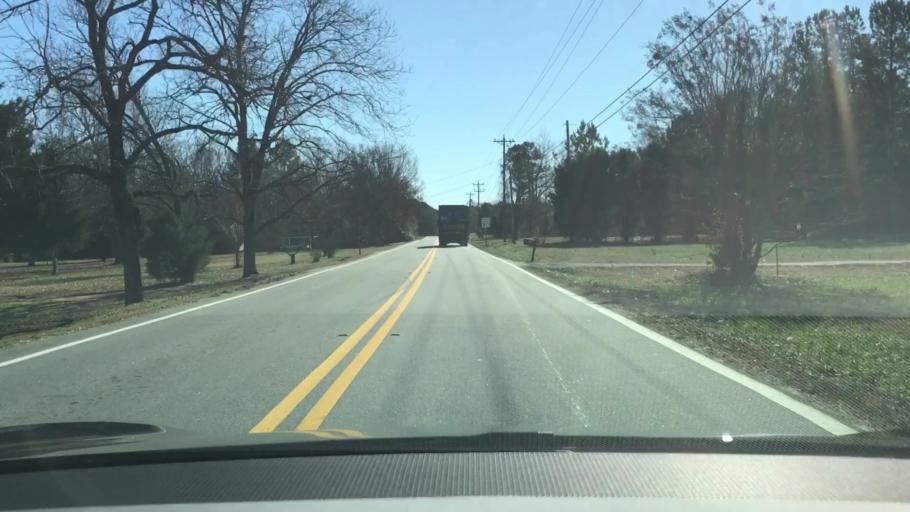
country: US
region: Georgia
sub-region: Gwinnett County
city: Dacula
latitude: 33.9471
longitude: -83.8445
